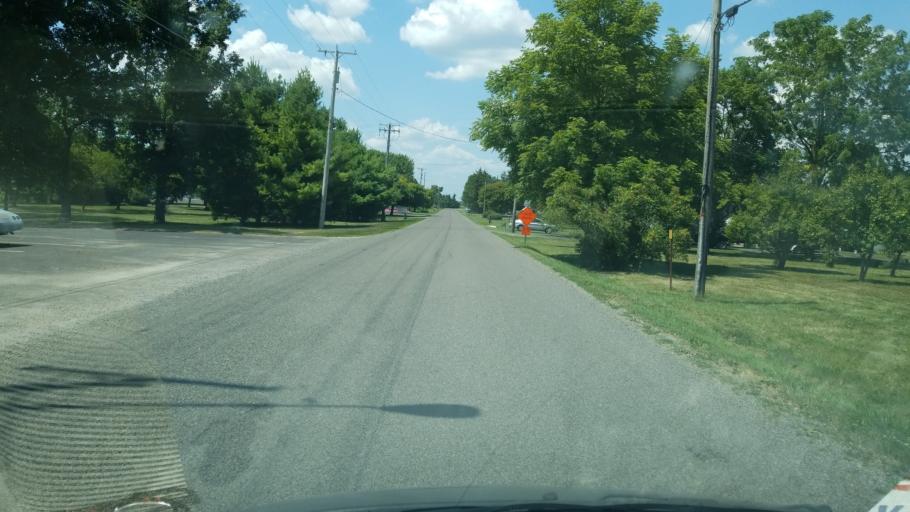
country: US
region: Ohio
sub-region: Champaign County
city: Mechanicsburg
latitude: 40.0785
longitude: -83.4552
